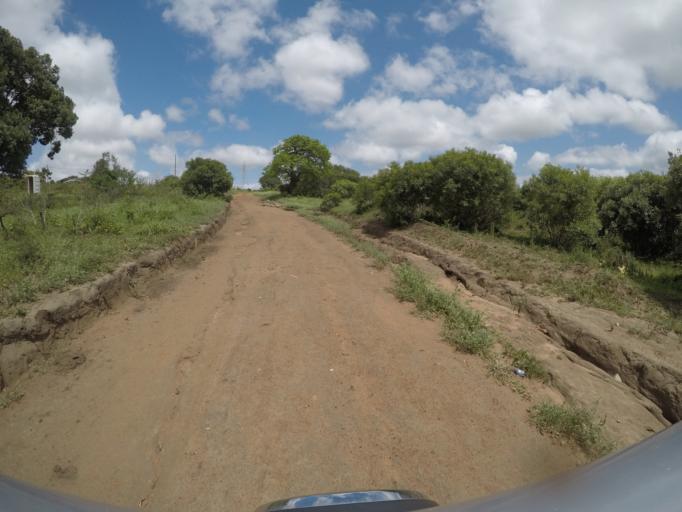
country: ZA
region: KwaZulu-Natal
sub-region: uThungulu District Municipality
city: Empangeni
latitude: -28.5826
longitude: 31.8352
